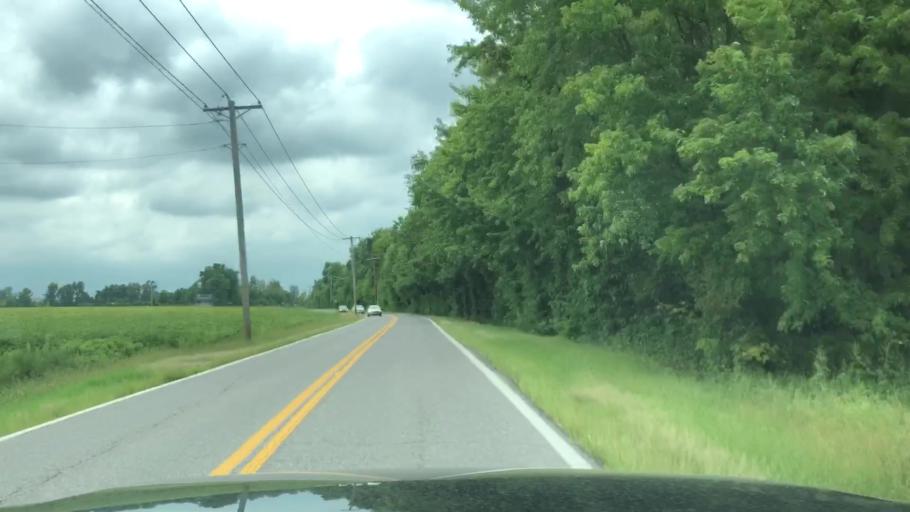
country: US
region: Missouri
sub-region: Saint Louis County
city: Bridgeton
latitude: 38.8091
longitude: -90.3991
